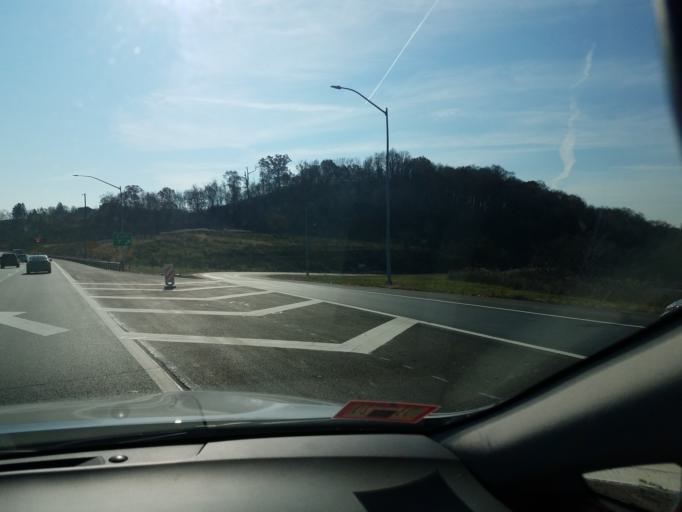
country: US
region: Pennsylvania
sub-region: Allegheny County
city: West View
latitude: 40.5151
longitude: -80.0525
